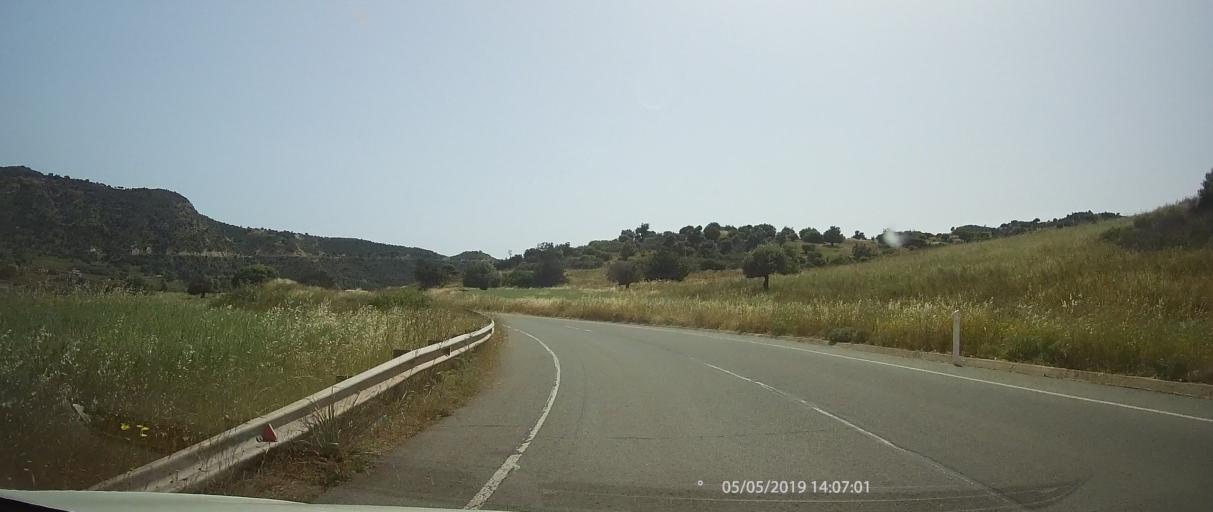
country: CY
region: Limassol
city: Pissouri
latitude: 34.7392
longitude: 32.6019
